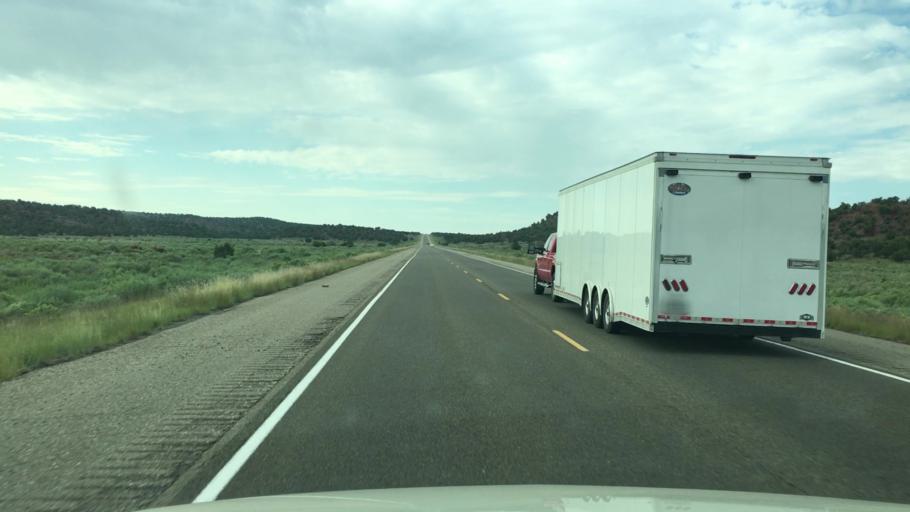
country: US
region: New Mexico
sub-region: Santa Fe County
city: Eldorado at Santa Fe
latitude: 35.2445
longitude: -105.8062
